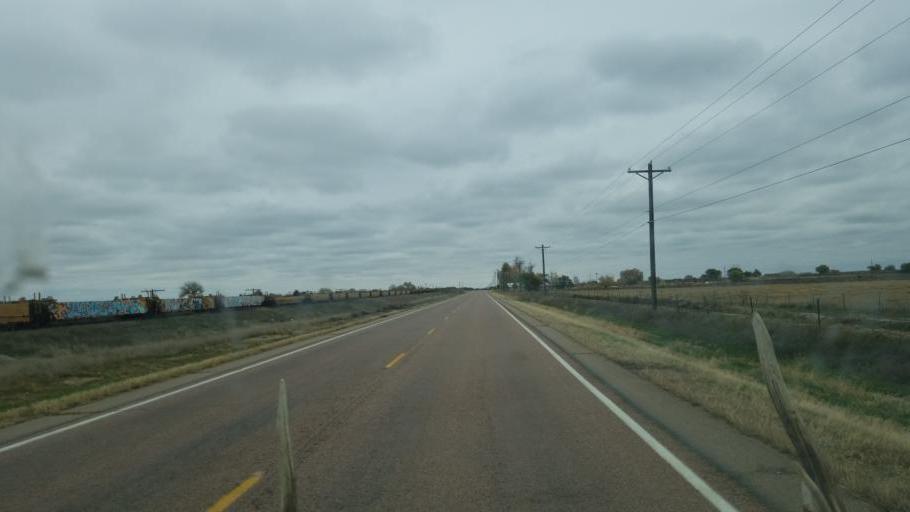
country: US
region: Colorado
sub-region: Crowley County
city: Ordway
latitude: 38.1851
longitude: -103.8804
